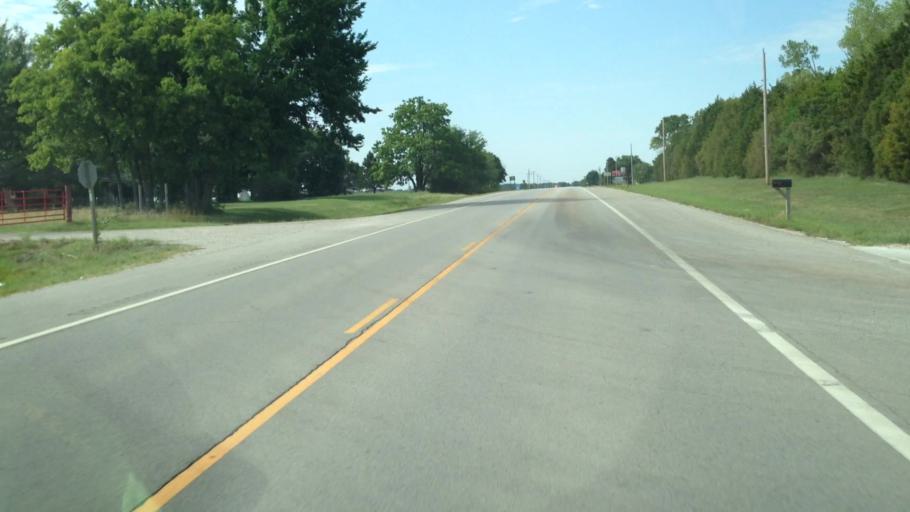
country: US
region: Kansas
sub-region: Labette County
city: Parsons
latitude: 37.3063
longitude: -95.2675
